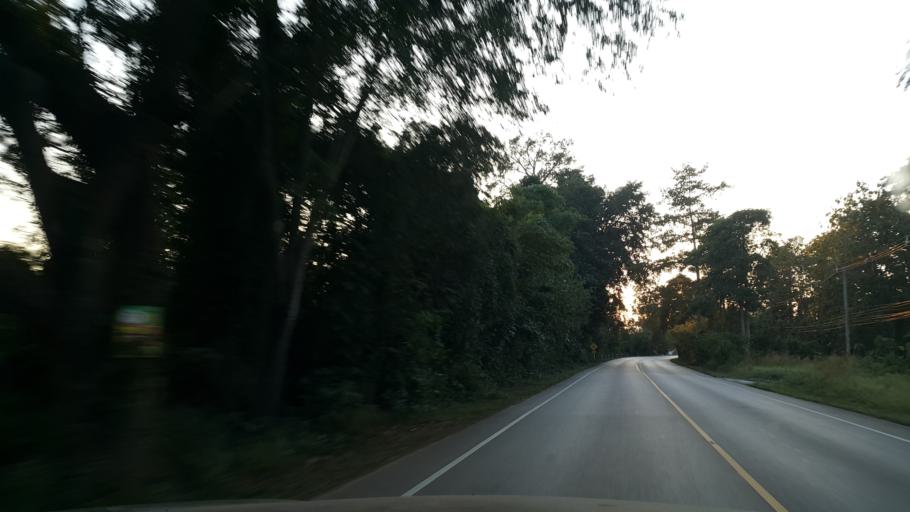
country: TH
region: Phrae
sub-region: Amphoe Wang Chin
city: Wang Chin
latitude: 17.8464
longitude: 99.6343
